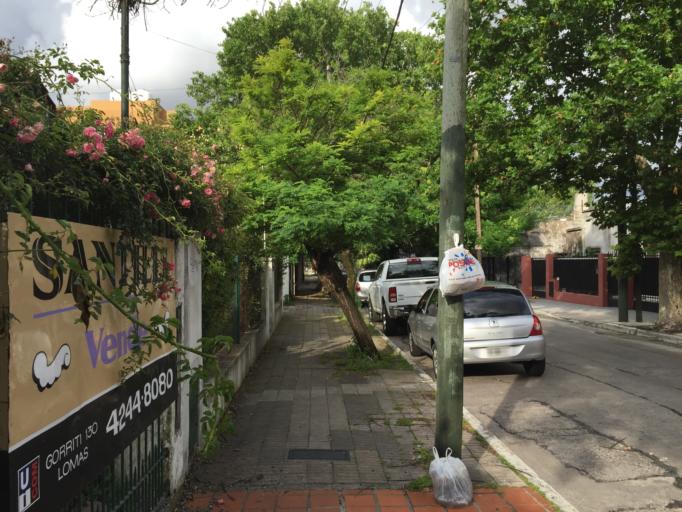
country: AR
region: Buenos Aires
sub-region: Partido de Lomas de Zamora
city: Lomas de Zamora
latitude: -34.7796
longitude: -58.3980
